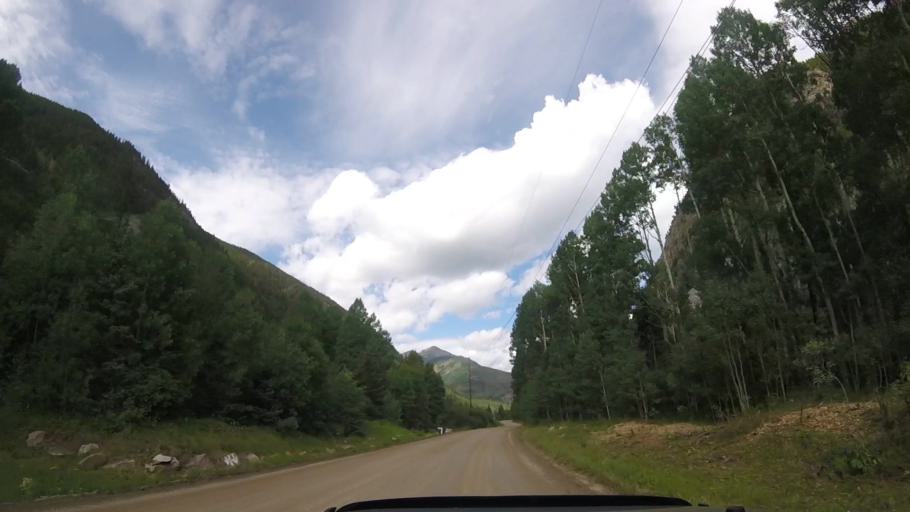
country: US
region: Colorado
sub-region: San Miguel County
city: Mountain Village
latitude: 37.8583
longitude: -107.8605
